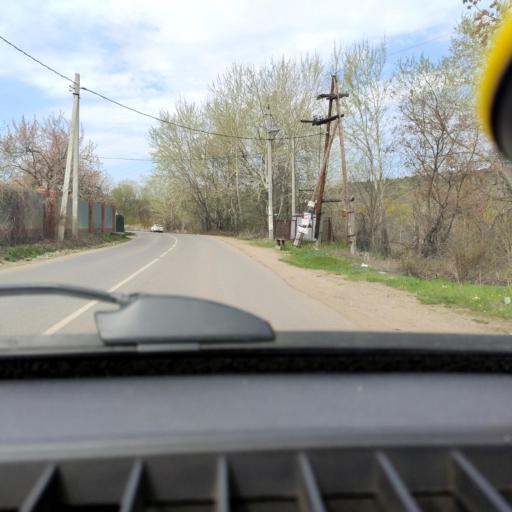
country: RU
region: Samara
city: Povolzhskiy
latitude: 53.4654
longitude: 49.6672
